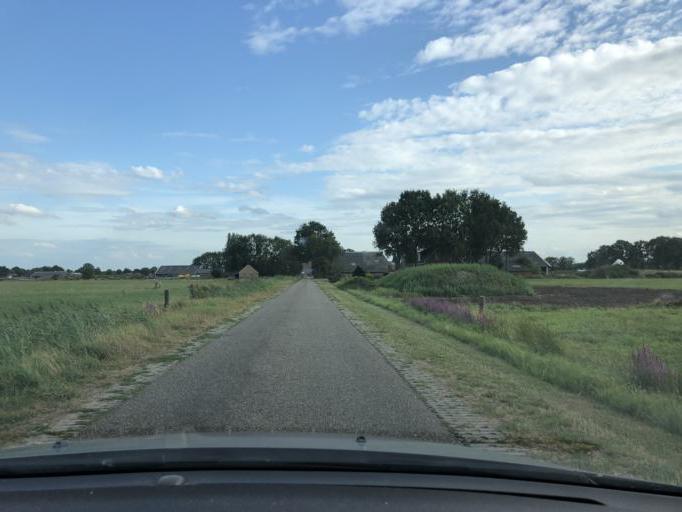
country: NL
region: Overijssel
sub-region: Gemeente Dalfsen
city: Dalfsen
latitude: 52.6022
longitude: 6.3454
